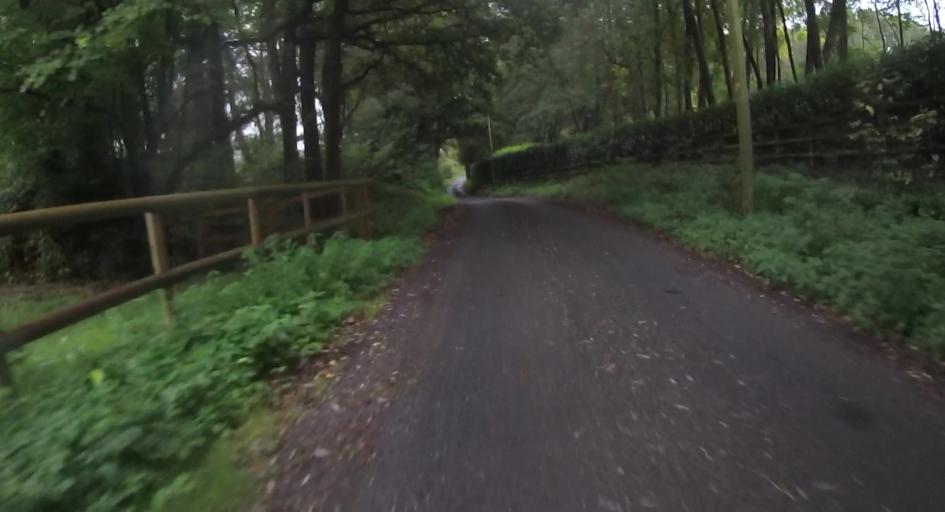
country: GB
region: England
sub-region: Hampshire
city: Tadley
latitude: 51.3531
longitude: -1.1773
